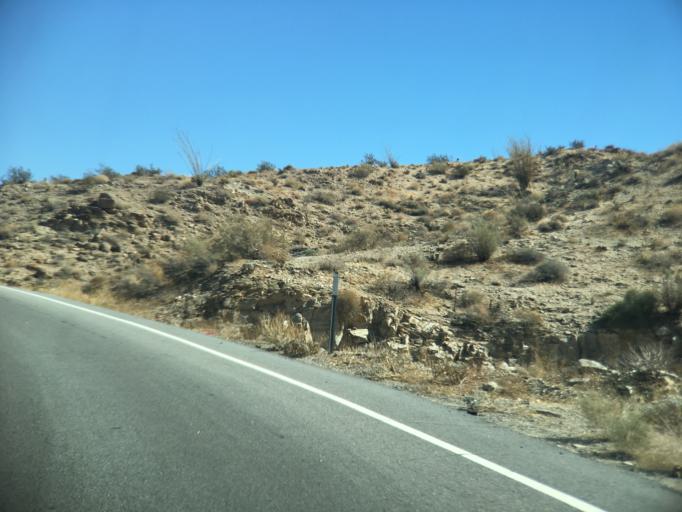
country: US
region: California
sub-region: Riverside County
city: Palm Desert
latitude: 33.6581
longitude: -116.4006
